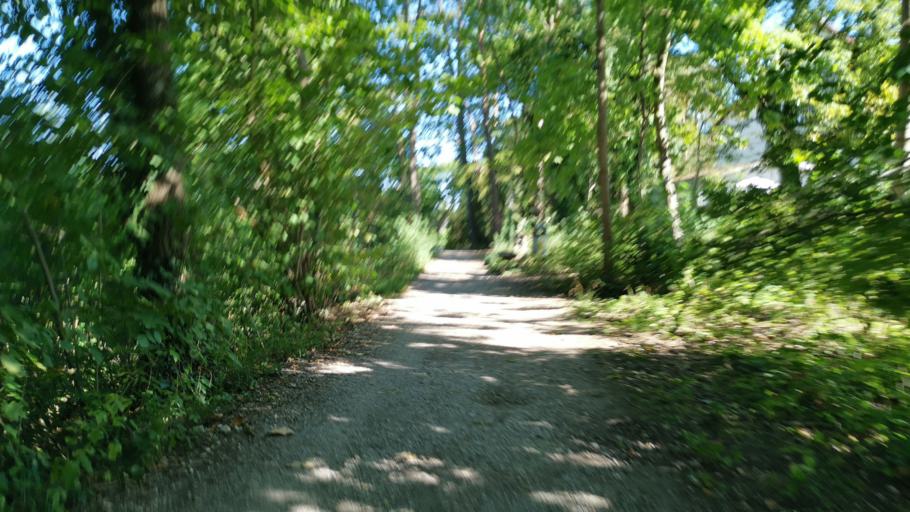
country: DE
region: Bavaria
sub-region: Upper Bavaria
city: Pullach im Isartal
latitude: 48.0738
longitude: 11.5345
